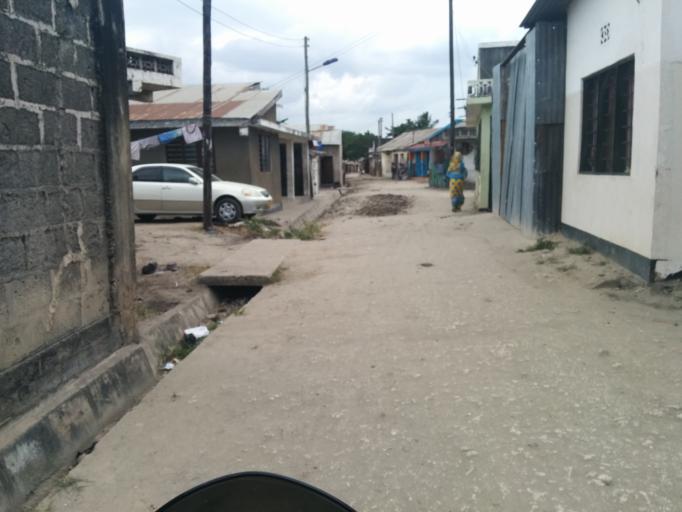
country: TZ
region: Dar es Salaam
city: Dar es Salaam
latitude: -6.8606
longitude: 39.2529
